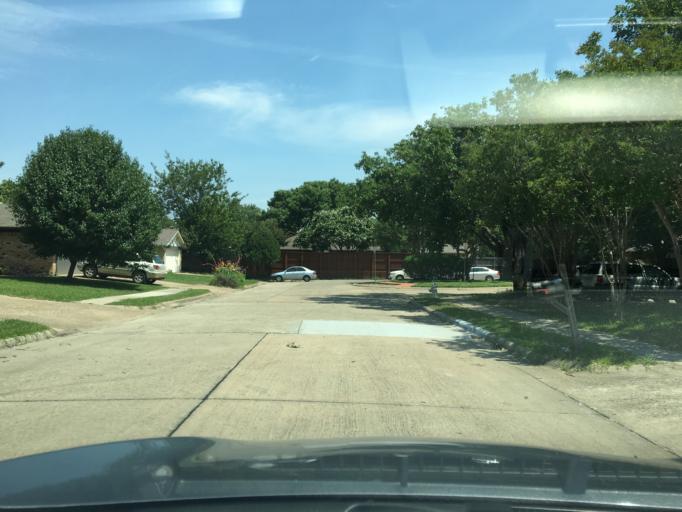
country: US
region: Texas
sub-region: Dallas County
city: Richardson
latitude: 32.9635
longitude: -96.6975
